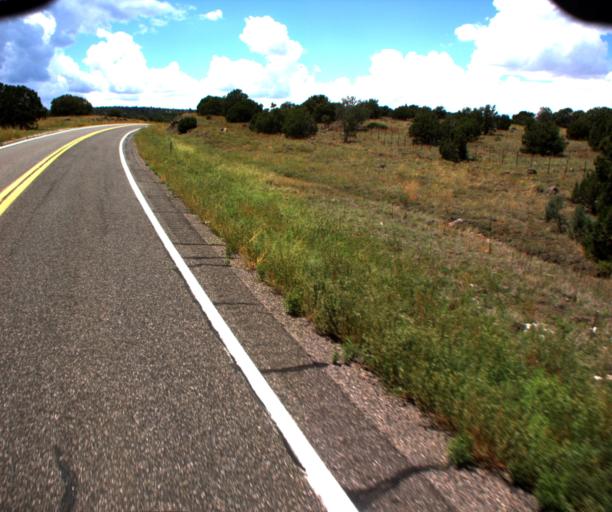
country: US
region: Arizona
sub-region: Gila County
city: Pine
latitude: 34.4881
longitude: -111.5997
